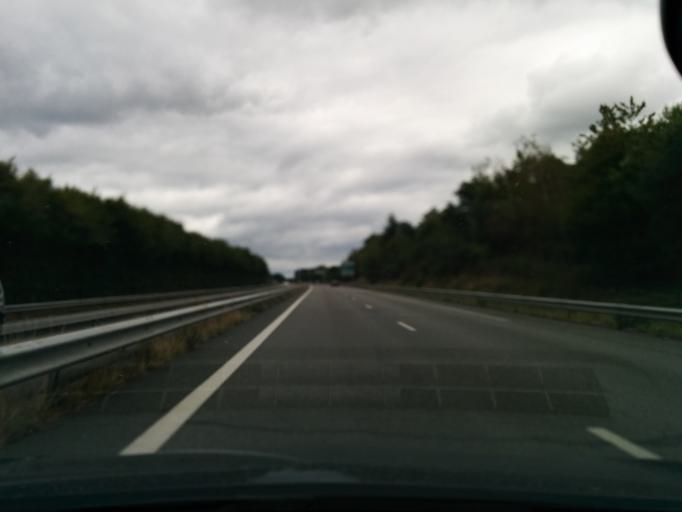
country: FR
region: Limousin
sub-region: Departement de la Creuse
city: Saint-Maurice-la-Souterraine
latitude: 46.1836
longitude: 1.3807
